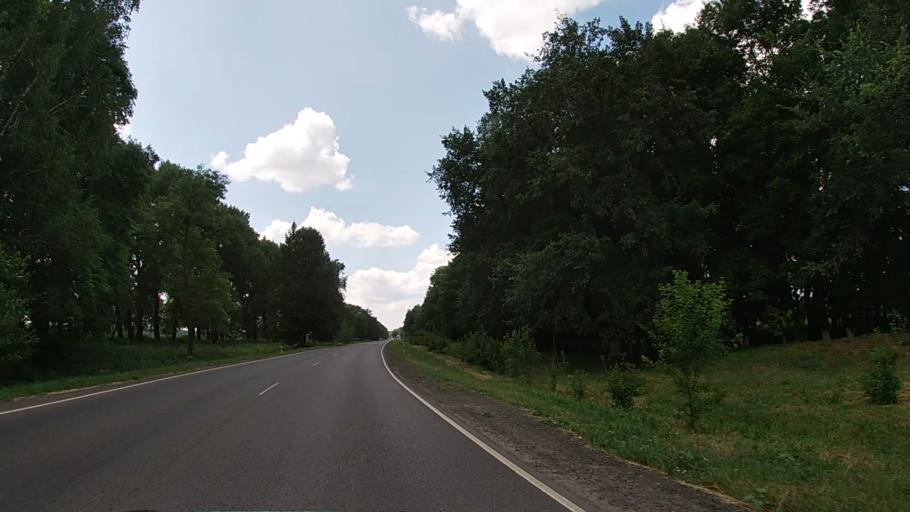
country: RU
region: Belgorod
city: Grayvoron
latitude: 50.4957
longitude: 35.7124
